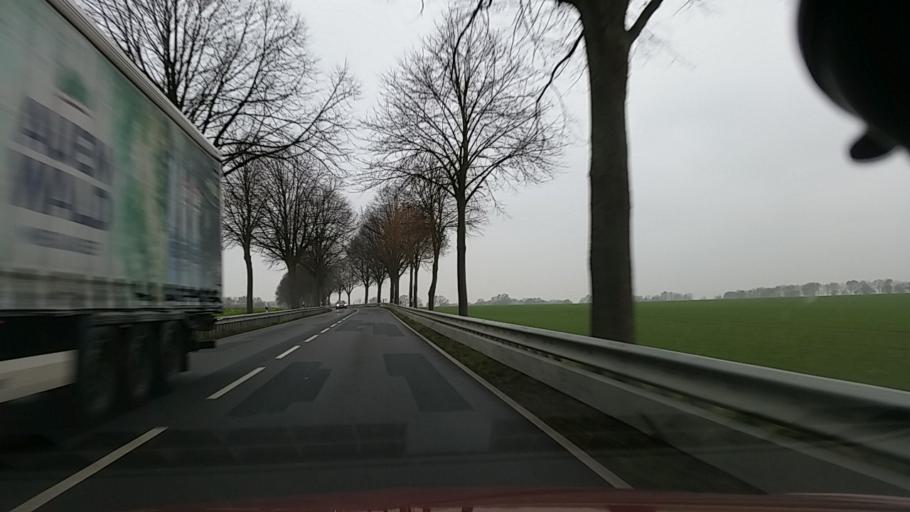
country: DE
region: Lower Saxony
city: Hankensbuttel
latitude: 52.7318
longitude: 10.6342
